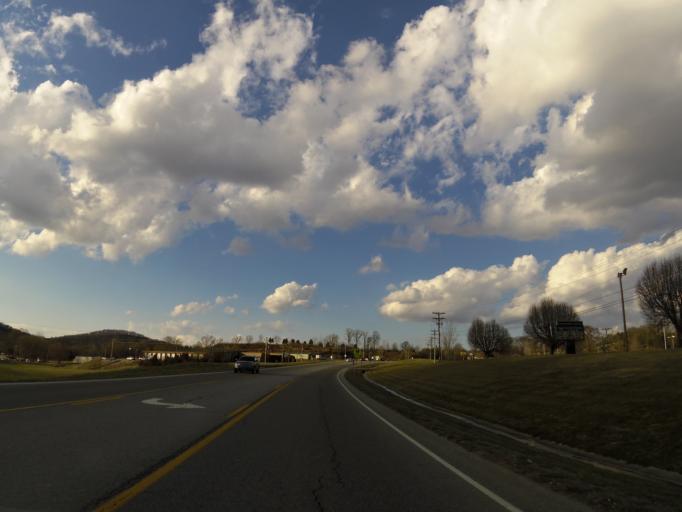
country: US
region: Tennessee
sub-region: Smith County
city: South Carthage
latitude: 36.2233
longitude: -85.9489
